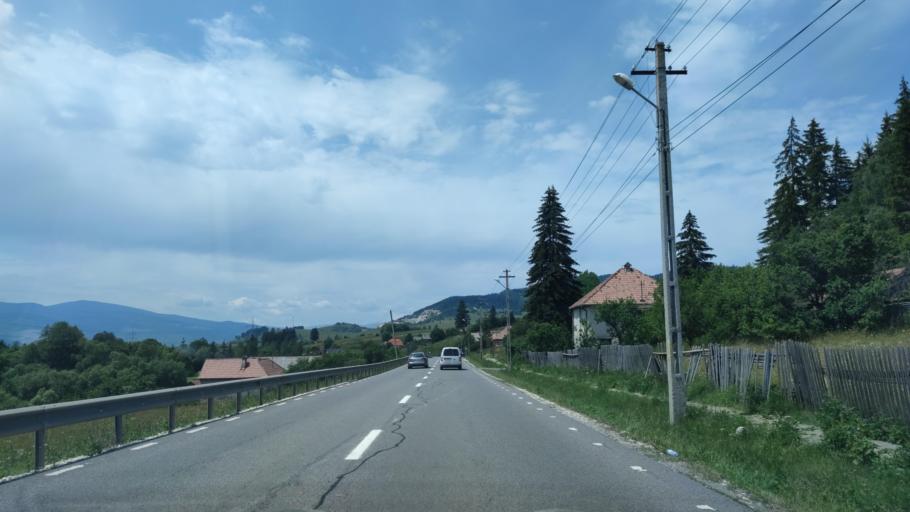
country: RO
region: Harghita
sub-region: Comuna Voslobeni
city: Voslobeni
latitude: 46.6273
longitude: 25.6770
